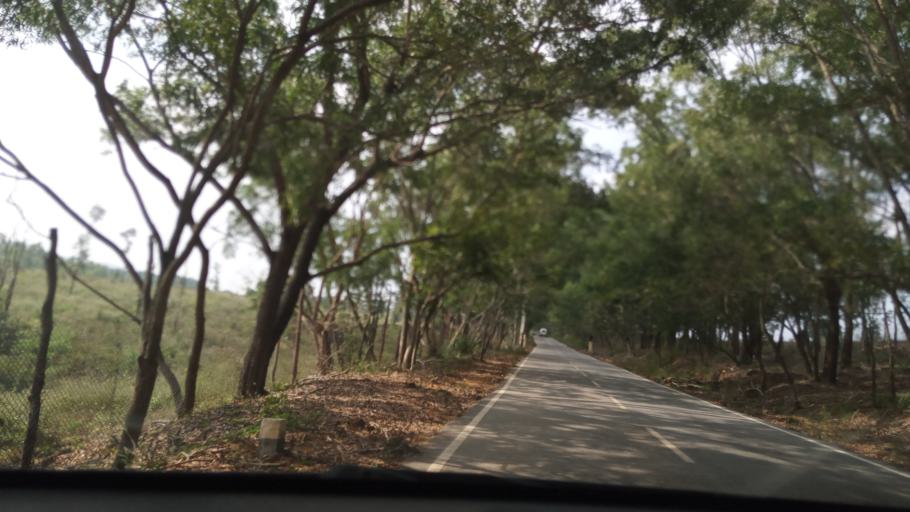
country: IN
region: Andhra Pradesh
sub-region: Chittoor
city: Tirumala
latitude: 13.6997
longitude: 79.3495
